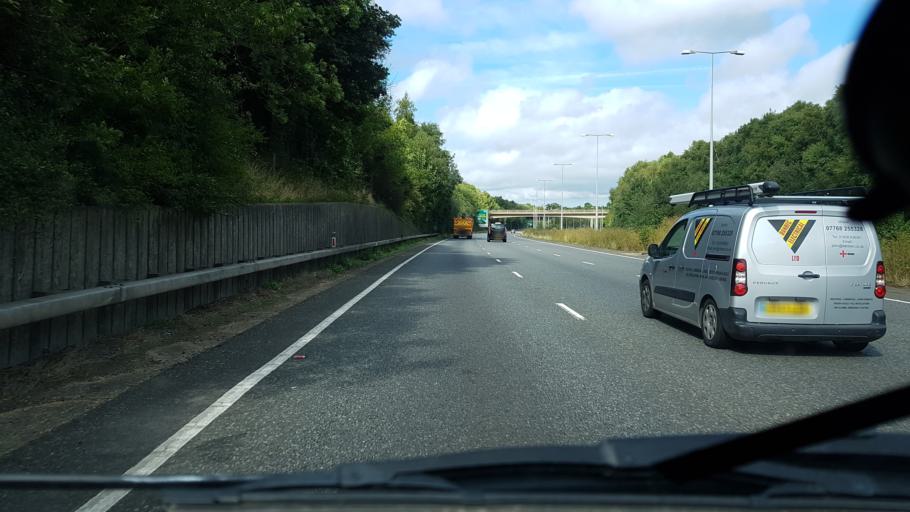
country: GB
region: England
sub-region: West Sussex
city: Broadfield
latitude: 51.0808
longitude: -0.2029
